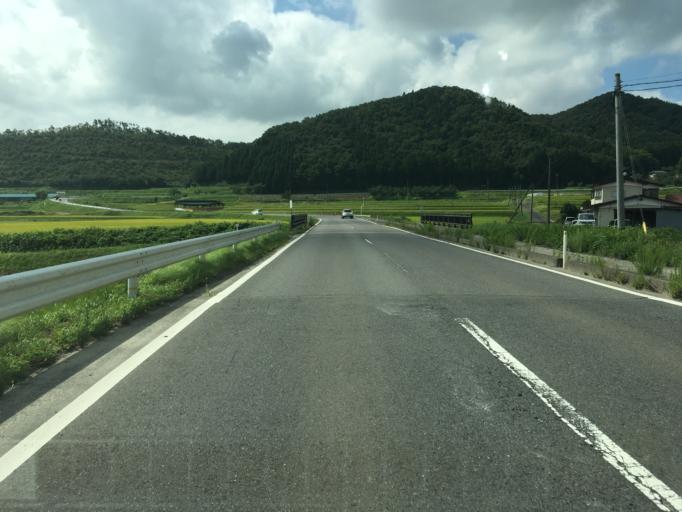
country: JP
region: Fukushima
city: Motomiya
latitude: 37.5209
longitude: 140.3729
